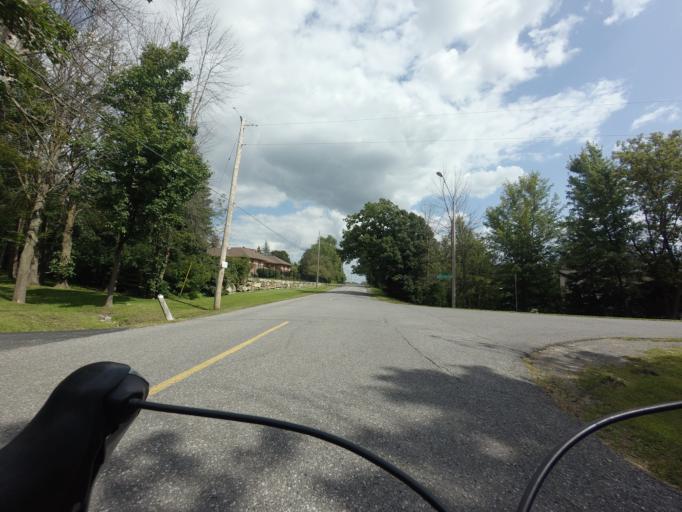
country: CA
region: Ontario
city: Bells Corners
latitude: 45.2647
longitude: -75.8200
